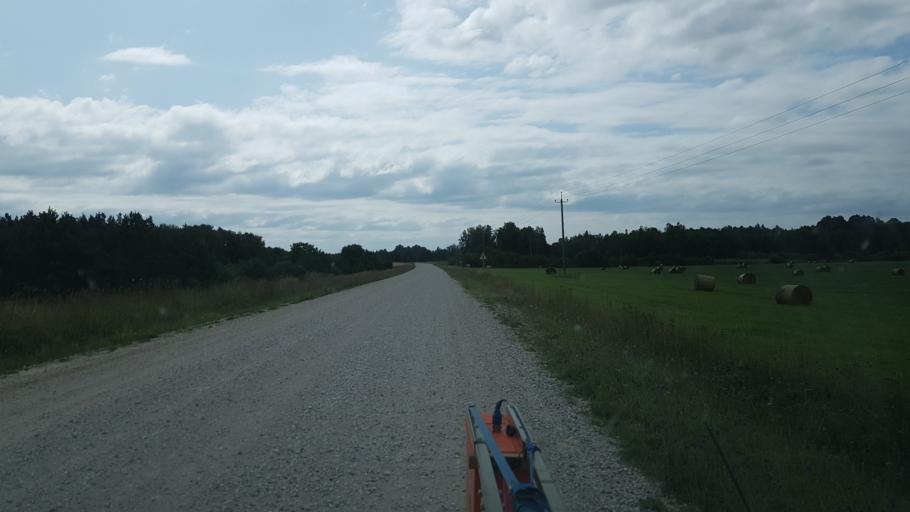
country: EE
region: Paernumaa
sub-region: Halinga vald
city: Parnu-Jaagupi
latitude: 58.5688
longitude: 24.4100
